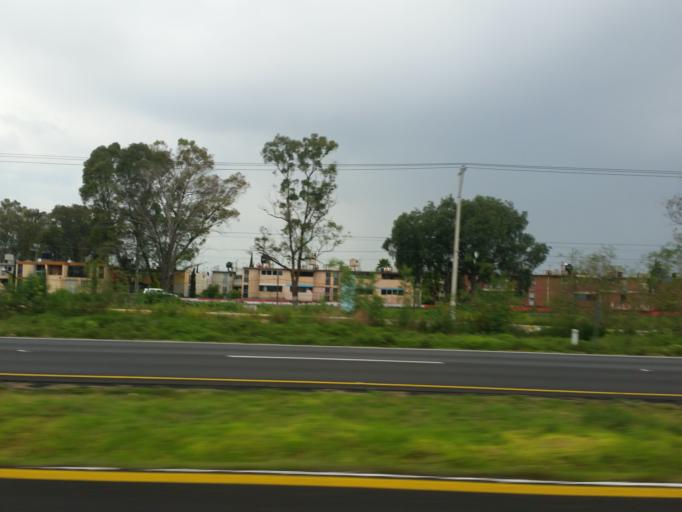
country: MX
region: Mexico
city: Santo Tomas Chiconautla
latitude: 19.6138
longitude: -99.0184
